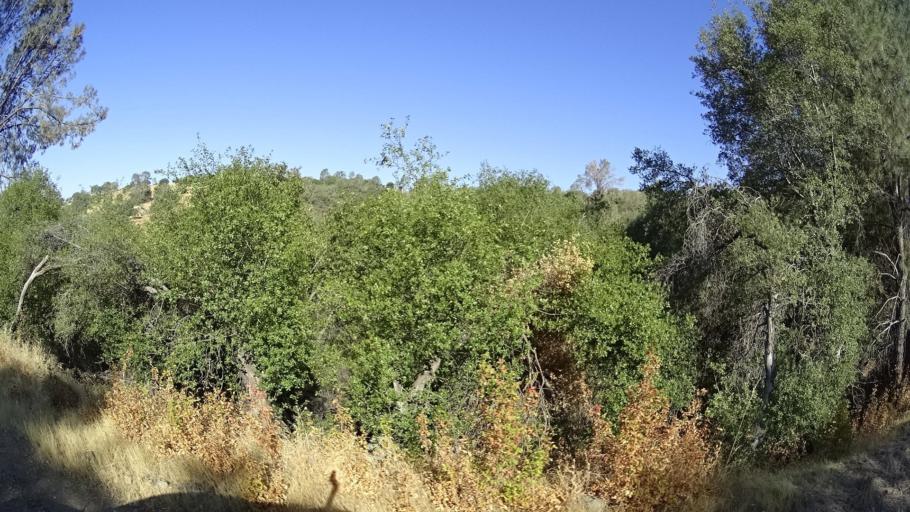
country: US
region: California
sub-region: Mariposa County
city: Mariposa
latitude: 37.5629
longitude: -120.1706
